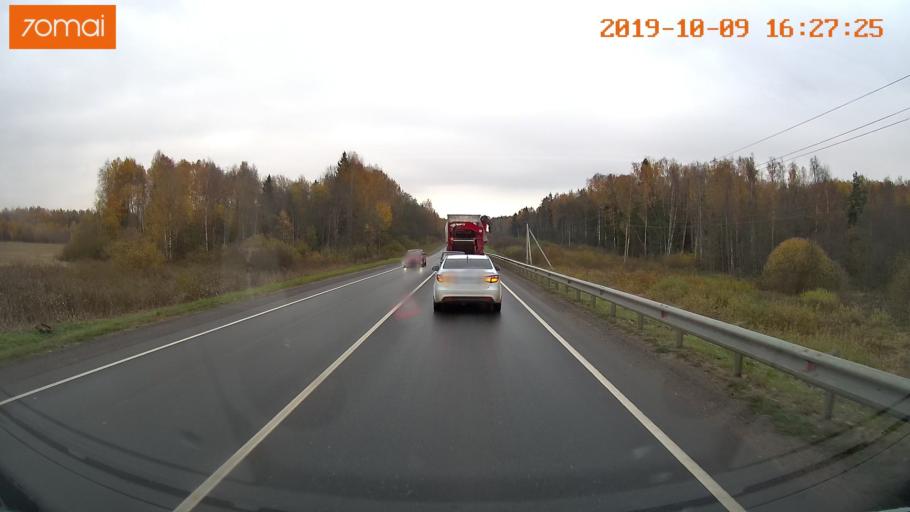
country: RU
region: Kostroma
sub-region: Kostromskoy Rayon
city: Kostroma
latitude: 57.6333
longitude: 40.9280
